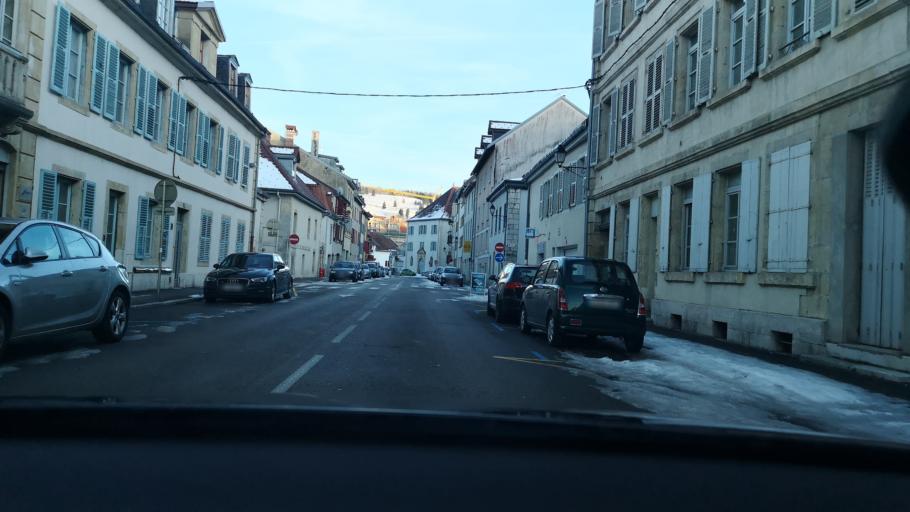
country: FR
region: Franche-Comte
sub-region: Departement du Doubs
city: Pontarlier
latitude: 46.9039
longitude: 6.3573
